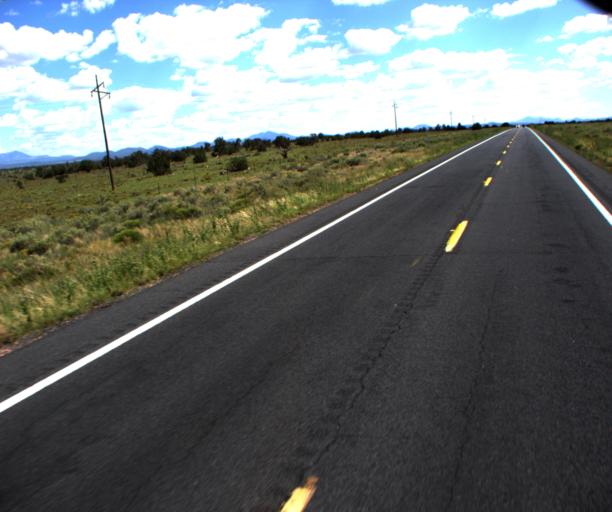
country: US
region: Arizona
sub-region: Coconino County
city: Grand Canyon Village
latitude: 35.6944
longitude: -112.1337
